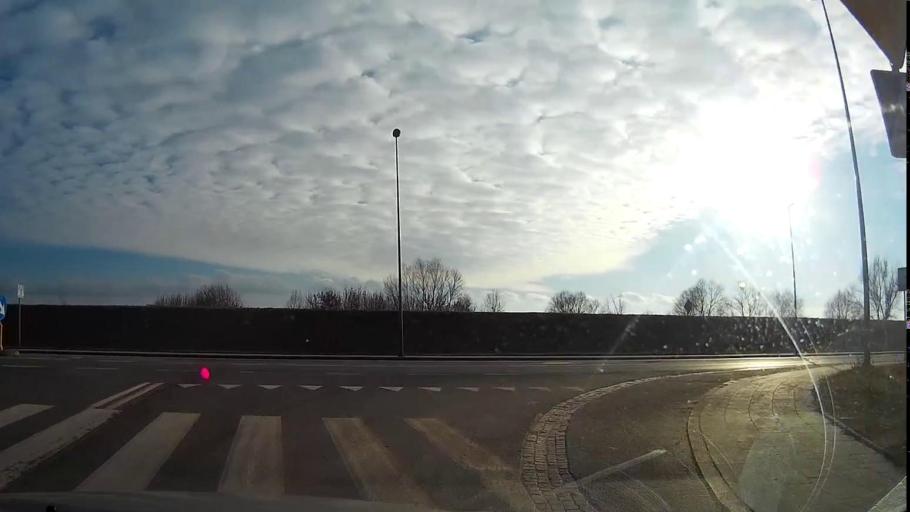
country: PL
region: Lesser Poland Voivodeship
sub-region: Powiat krakowski
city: Rzaska
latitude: 50.0451
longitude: 19.8596
